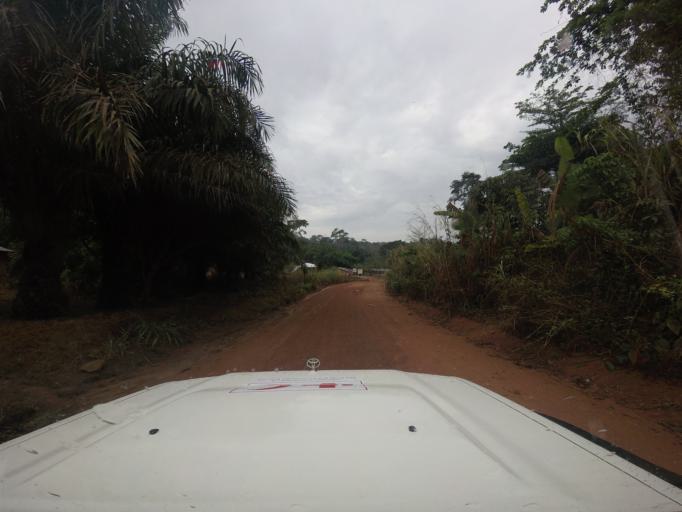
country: SL
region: Eastern Province
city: Buedu
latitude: 8.3362
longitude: -10.1688
